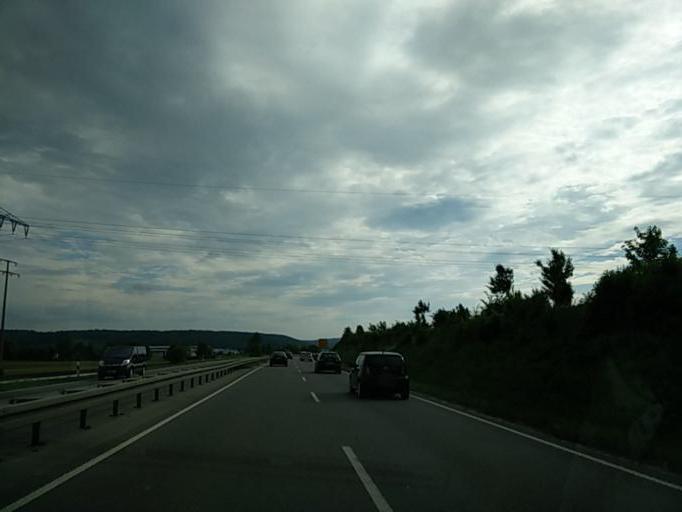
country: DE
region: Baden-Wuerttemberg
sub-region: Tuebingen Region
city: Tuebingen
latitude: 48.5038
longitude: 9.0369
